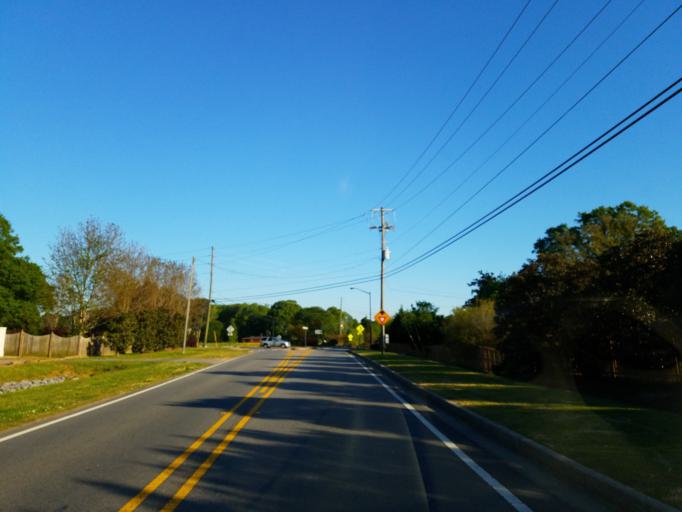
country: US
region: Georgia
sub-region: Cobb County
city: Powder Springs
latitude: 33.9278
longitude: -84.6384
